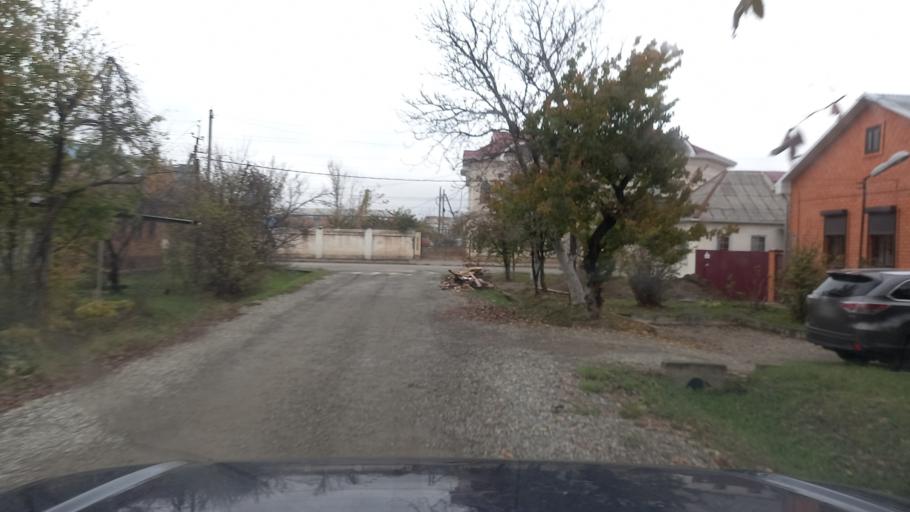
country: RU
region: Adygeya
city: Maykop
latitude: 44.6061
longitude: 40.0914
